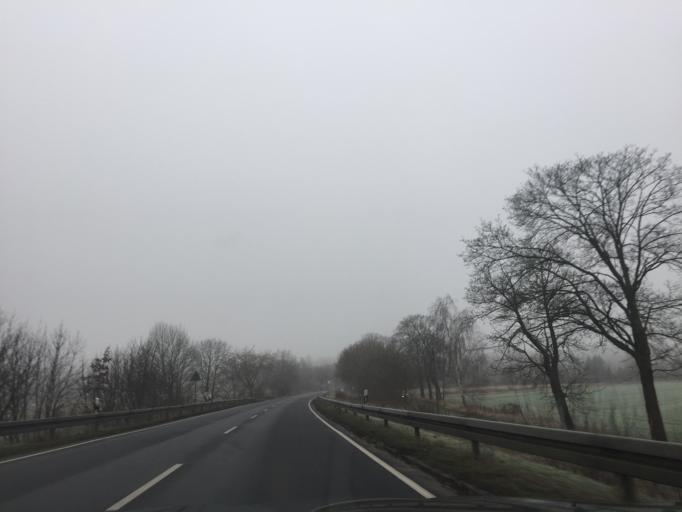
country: DE
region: Brandenburg
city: Hennigsdorf
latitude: 52.6389
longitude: 13.1489
